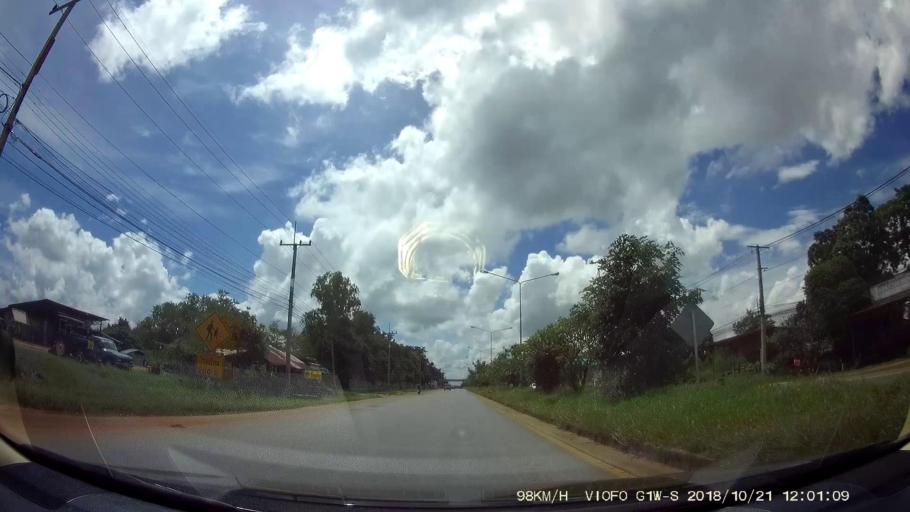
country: TH
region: Chaiyaphum
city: Chatturat
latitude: 15.5421
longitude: 101.8376
